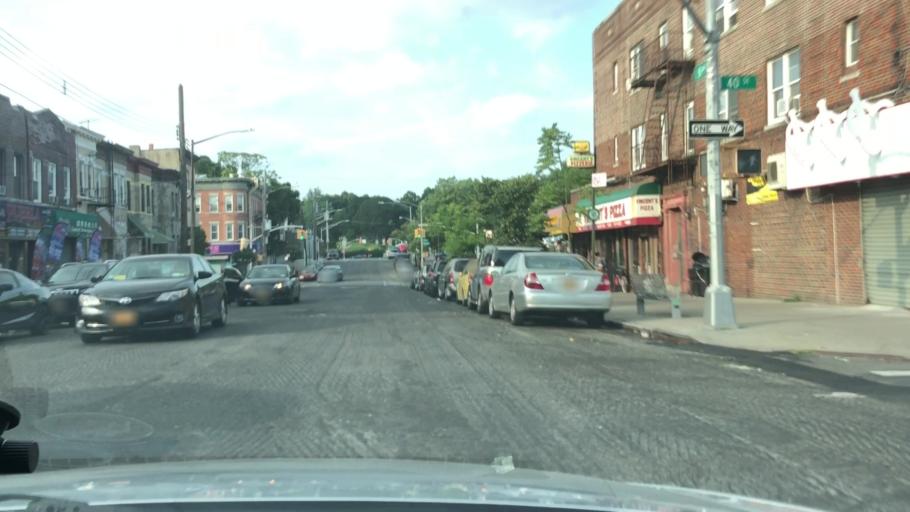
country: US
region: New York
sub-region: Kings County
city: Bensonhurst
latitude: 40.6453
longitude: -73.9958
